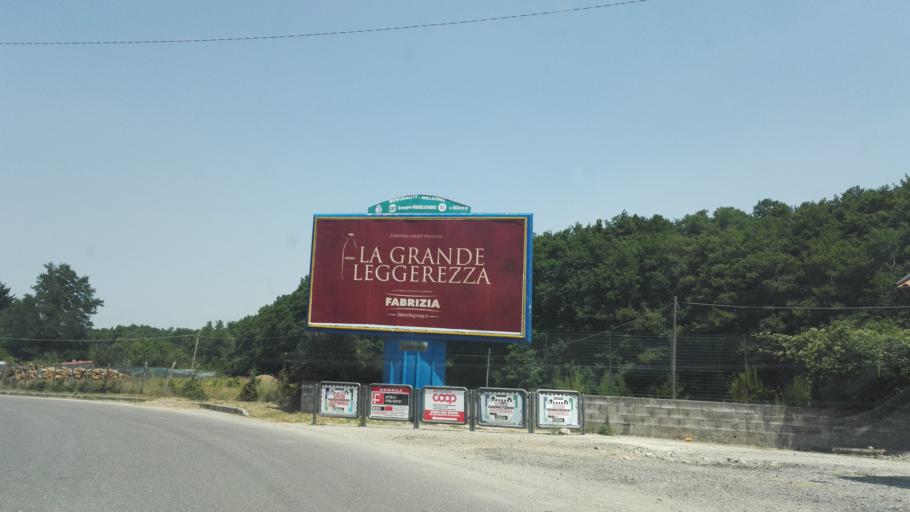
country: IT
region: Calabria
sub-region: Provincia di Vibo-Valentia
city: Serra San Bruno
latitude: 38.5653
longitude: 16.3288
